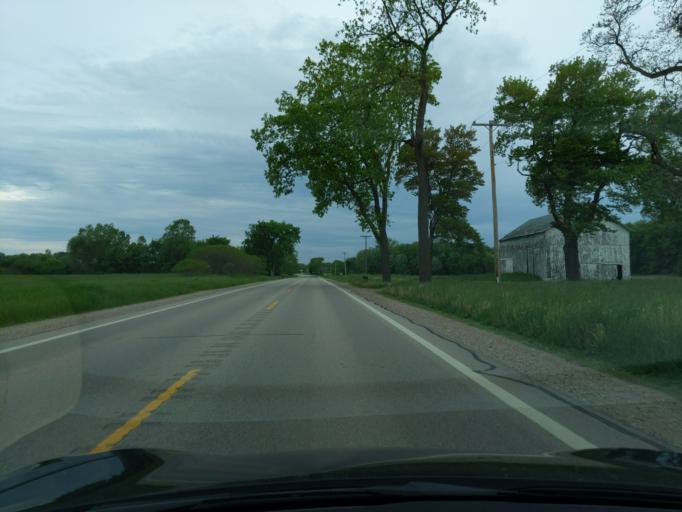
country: US
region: Michigan
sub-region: Jackson County
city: Michigan Center
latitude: 42.3478
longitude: -84.3398
